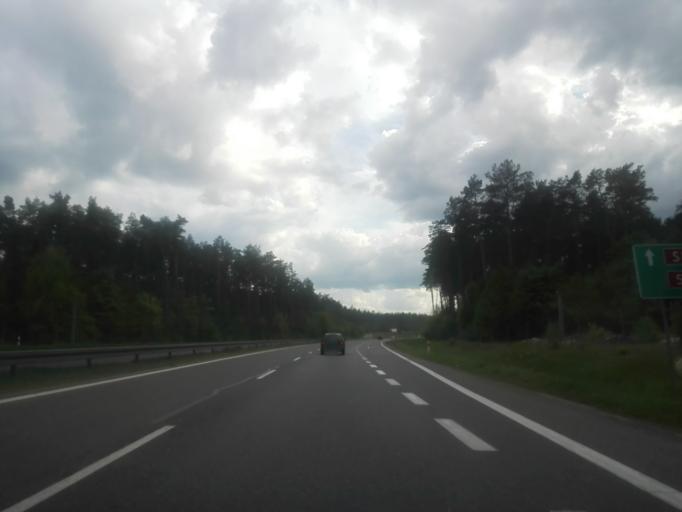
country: PL
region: Masovian Voivodeship
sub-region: Powiat ostrowski
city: Ostrow Mazowiecka
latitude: 52.7888
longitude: 21.8649
